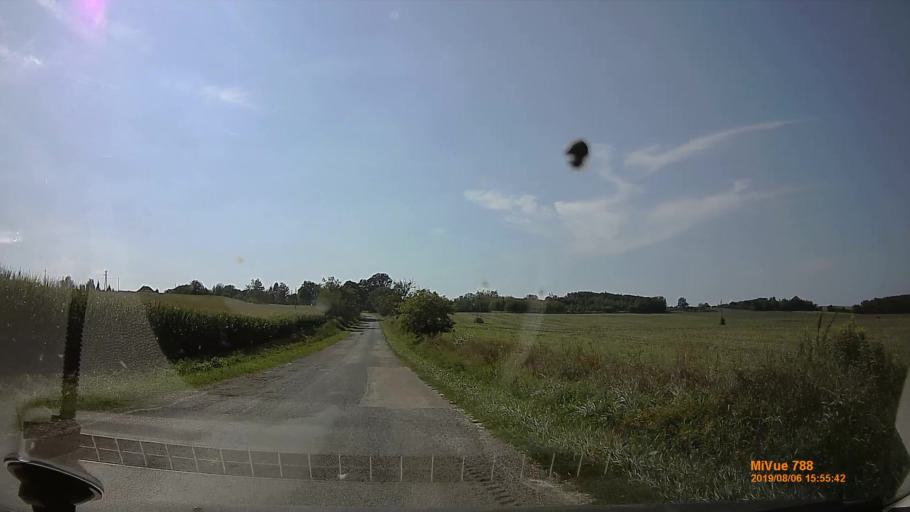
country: HU
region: Somogy
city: Csurgo
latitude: 46.2903
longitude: 17.0177
